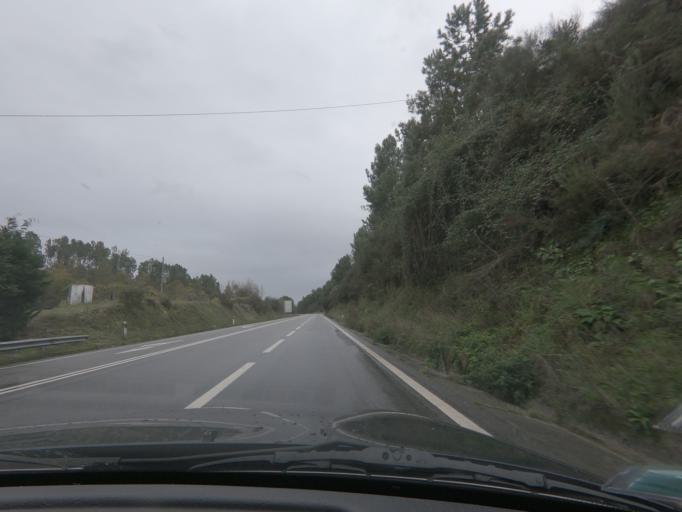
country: PT
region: Porto
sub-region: Amarante
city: Teloes
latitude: 41.3118
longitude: -8.0750
